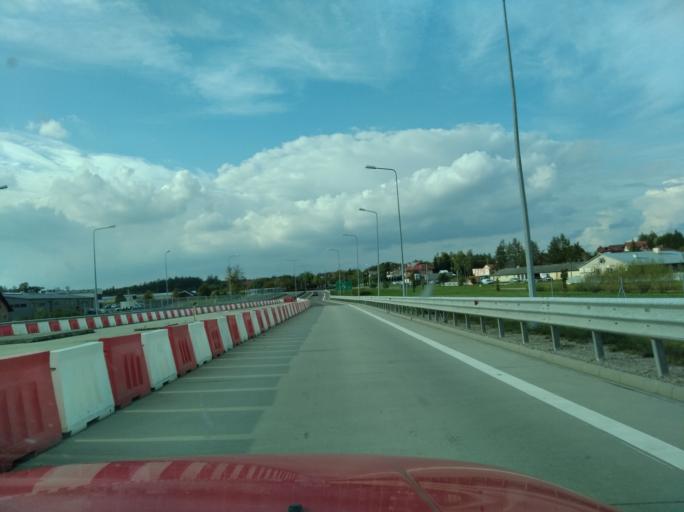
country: PL
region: Subcarpathian Voivodeship
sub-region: Powiat jaroslawski
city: Pawlosiow
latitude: 49.9758
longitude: 22.6442
